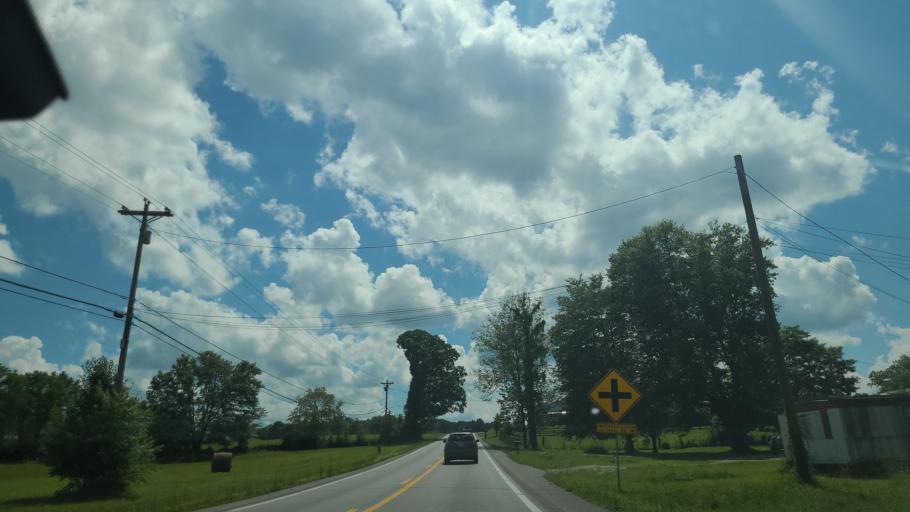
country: US
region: Kentucky
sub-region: Whitley County
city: Corbin
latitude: 36.9015
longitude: -84.1713
